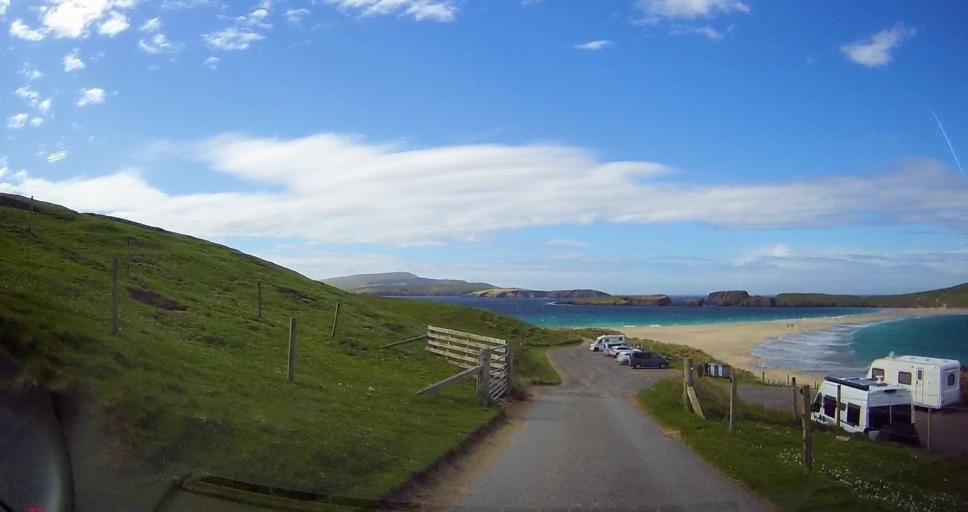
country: GB
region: Scotland
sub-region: Shetland Islands
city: Sandwick
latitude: 59.9715
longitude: -1.3300
